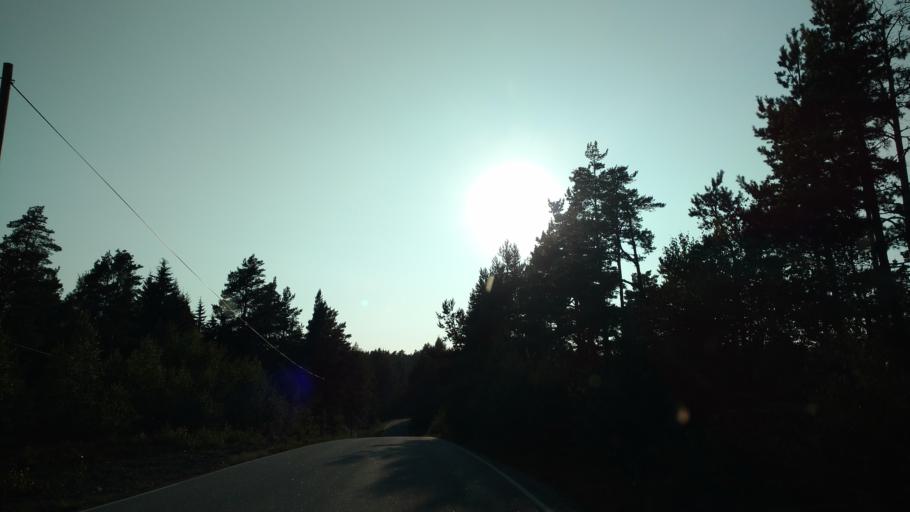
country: FI
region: Varsinais-Suomi
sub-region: Aboland-Turunmaa
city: Dragsfjaerd
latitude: 60.0282
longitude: 22.4610
